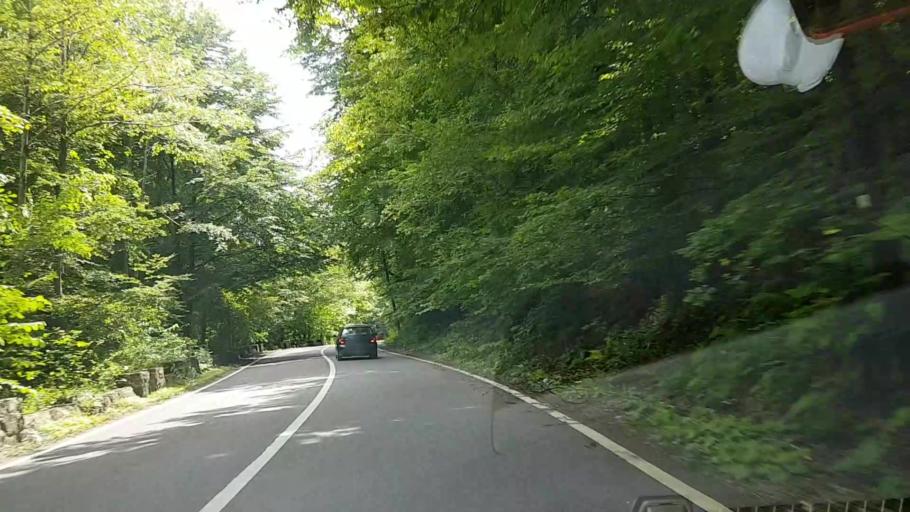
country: RO
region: Suceava
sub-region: Comuna Crucea
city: Crucea
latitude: 47.3052
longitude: 25.6271
